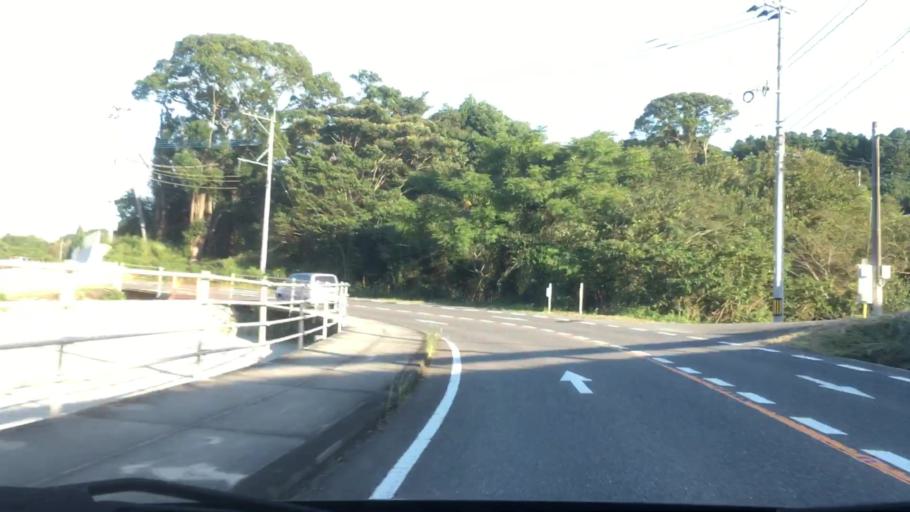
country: JP
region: Nagasaki
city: Sasebo
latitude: 33.0453
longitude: 129.7278
